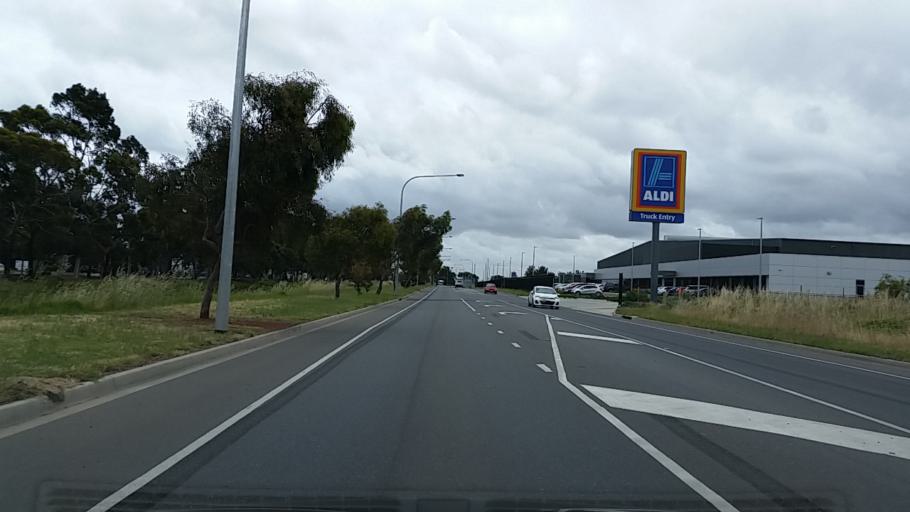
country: AU
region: South Australia
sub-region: Port Adelaide Enfield
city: Blair Athol
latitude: -34.8543
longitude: 138.5743
